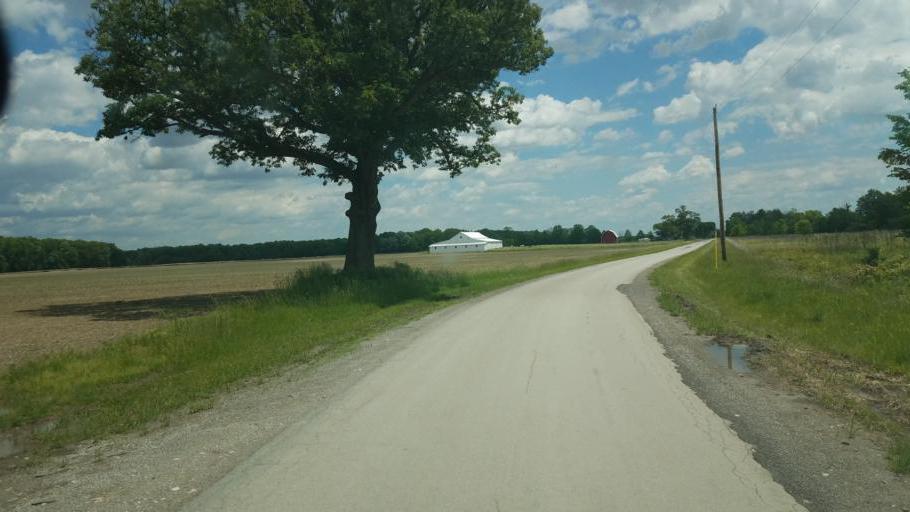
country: US
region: Ohio
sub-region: Wyandot County
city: Upper Sandusky
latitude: 40.7235
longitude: -83.3475
